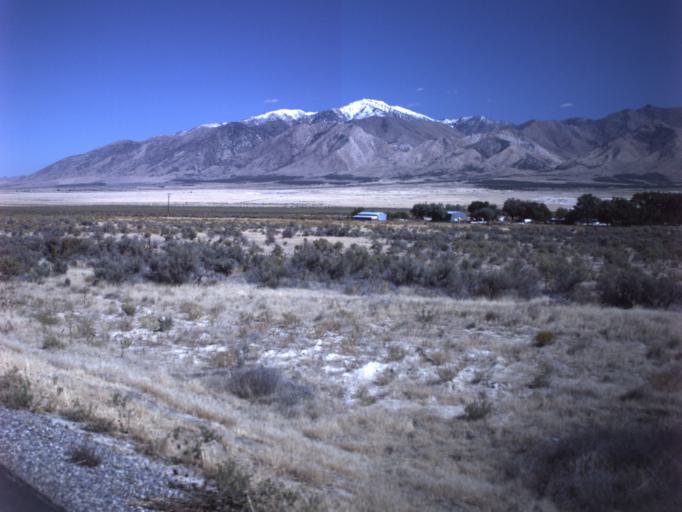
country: US
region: Utah
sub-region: Tooele County
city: Grantsville
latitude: 40.3400
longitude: -112.7448
